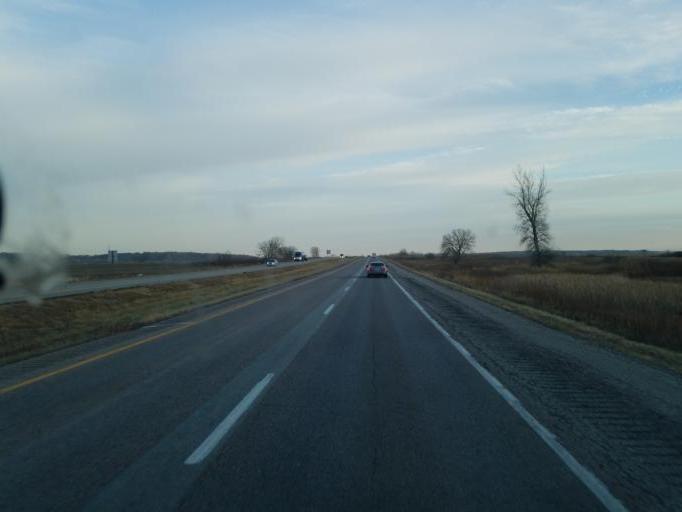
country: US
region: Iowa
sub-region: Harrison County
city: Missouri Valley
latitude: 41.5762
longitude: -95.9318
